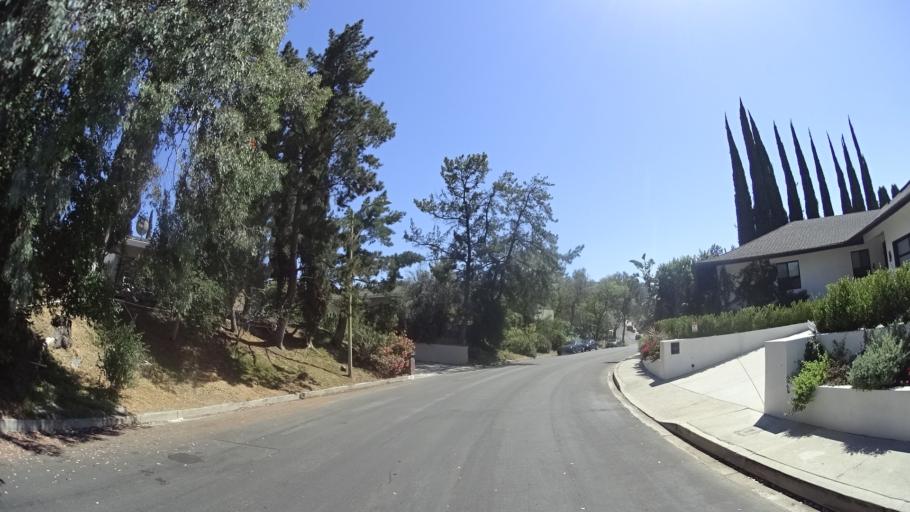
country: US
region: California
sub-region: Los Angeles County
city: Sherman Oaks
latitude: 34.1356
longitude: -118.4908
